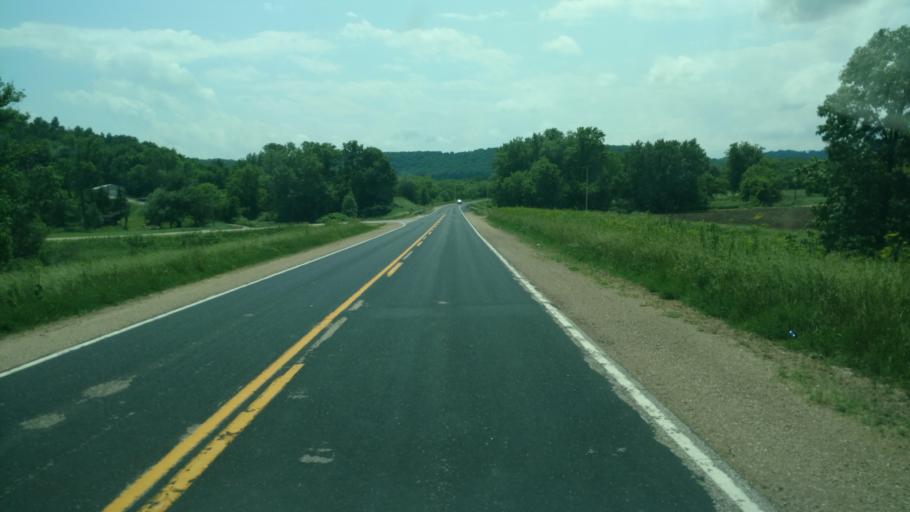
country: US
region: Wisconsin
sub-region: Monroe County
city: Cashton
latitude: 43.5634
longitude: -90.6404
